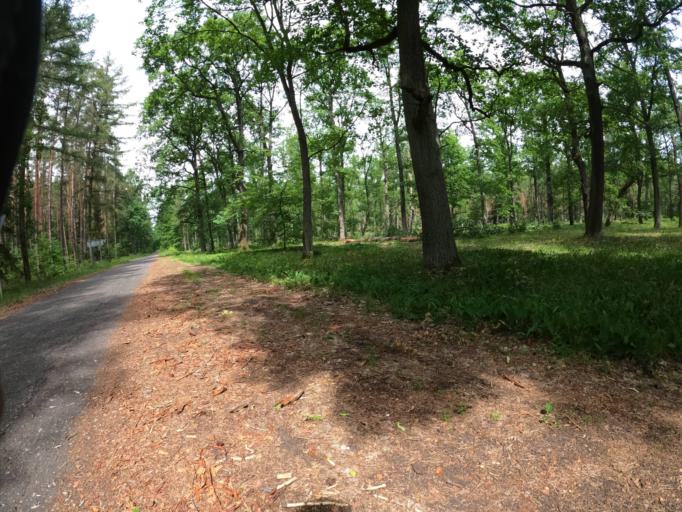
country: PL
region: West Pomeranian Voivodeship
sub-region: Powiat mysliborski
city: Boleszkowice
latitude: 52.6976
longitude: 14.5165
